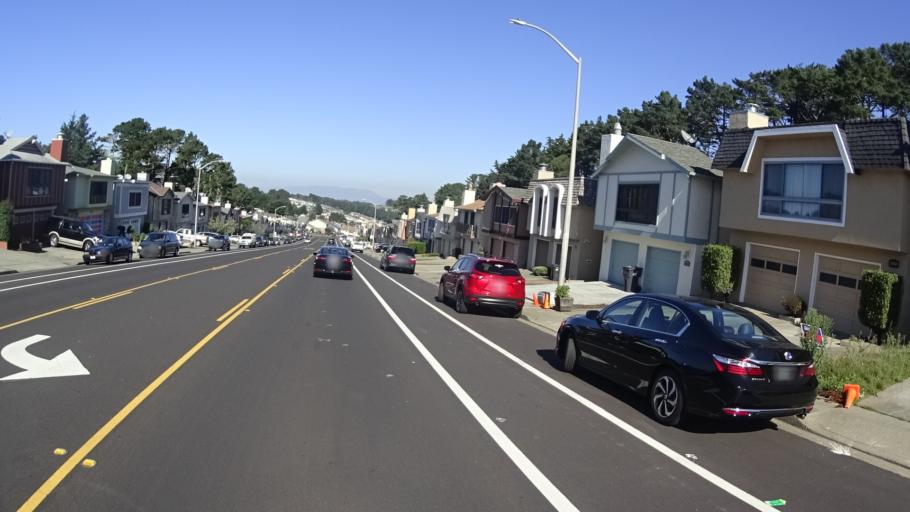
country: US
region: California
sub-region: San Mateo County
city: Colma
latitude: 37.6548
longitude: -122.4692
